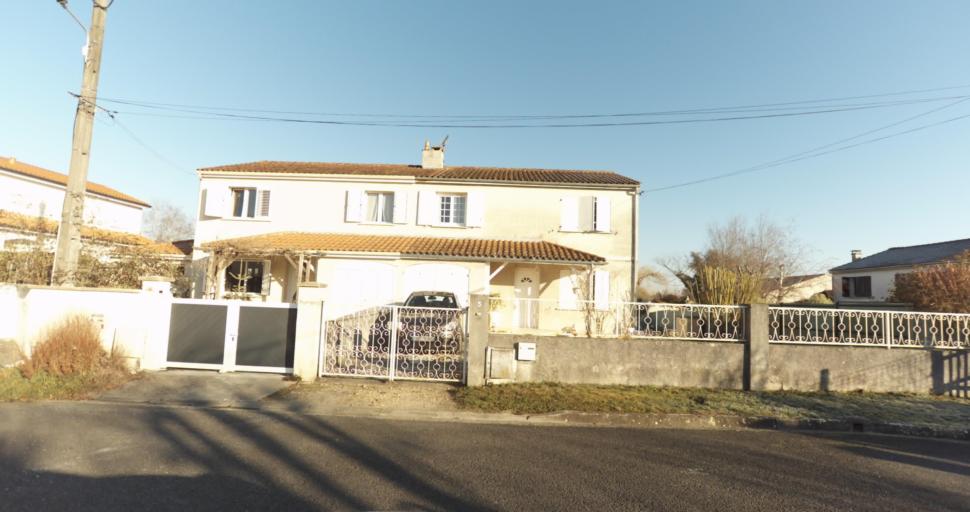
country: FR
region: Aquitaine
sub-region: Departement de la Gironde
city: Carbon-Blanc
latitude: 44.8962
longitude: -0.5066
